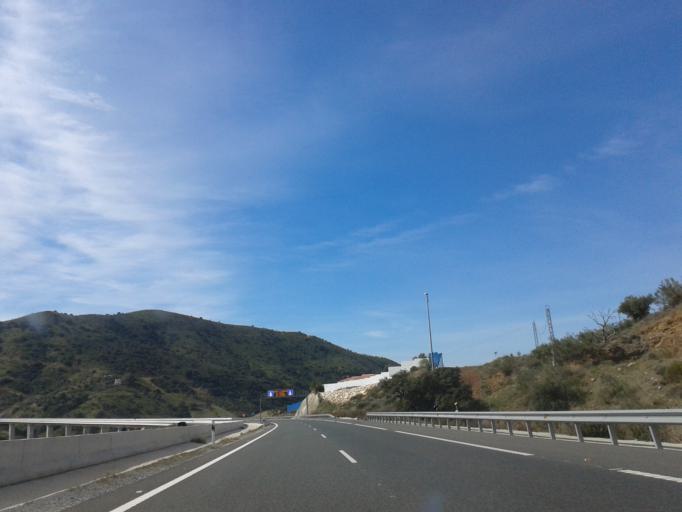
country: ES
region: Andalusia
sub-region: Provincia de Malaga
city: Casabermeja
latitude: 36.8800
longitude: -4.4778
